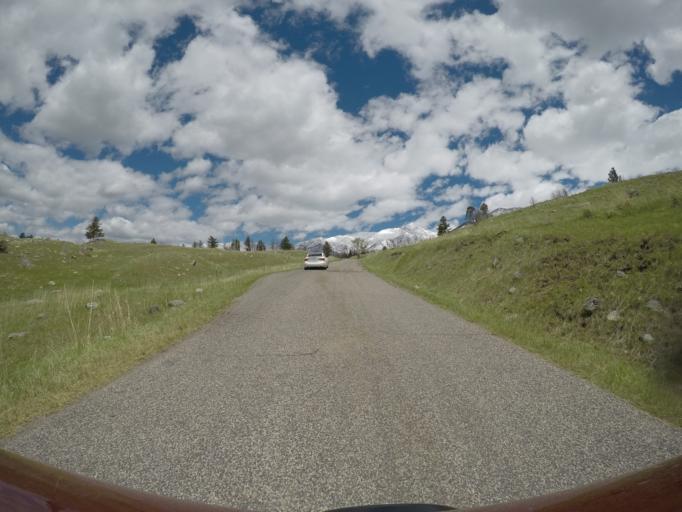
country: US
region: Montana
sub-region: Park County
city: Livingston
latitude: 45.4984
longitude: -110.5534
